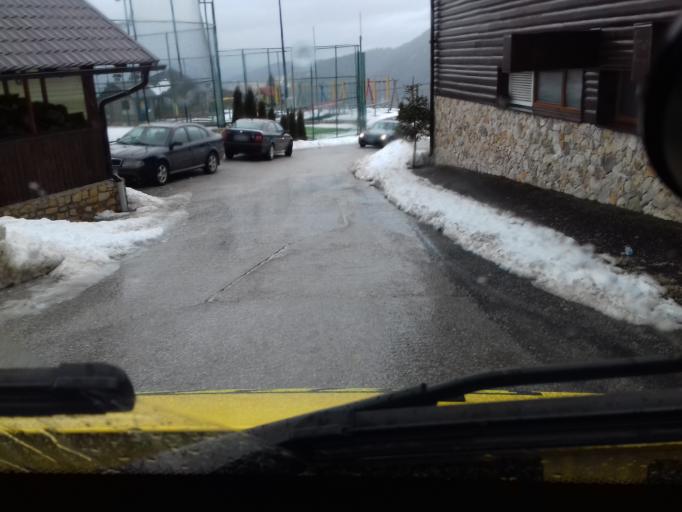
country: BA
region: Federation of Bosnia and Herzegovina
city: Turbe
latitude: 44.3138
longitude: 17.5824
